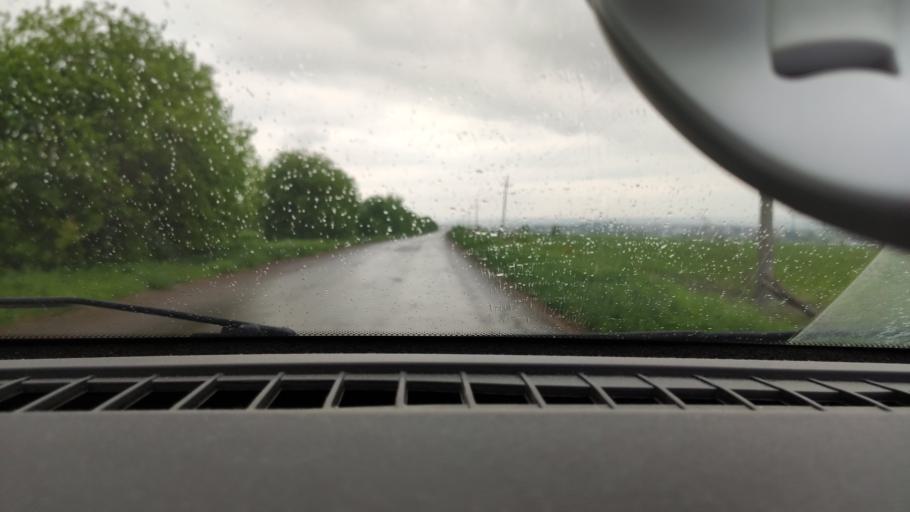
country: RU
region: Perm
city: Gamovo
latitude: 57.8545
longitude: 56.0811
